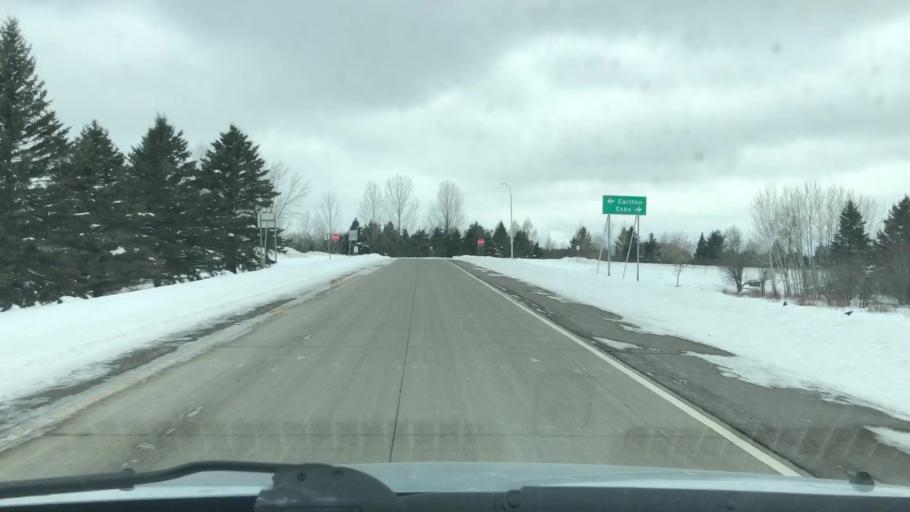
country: US
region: Minnesota
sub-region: Carlton County
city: Esko
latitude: 46.6969
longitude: -92.3637
